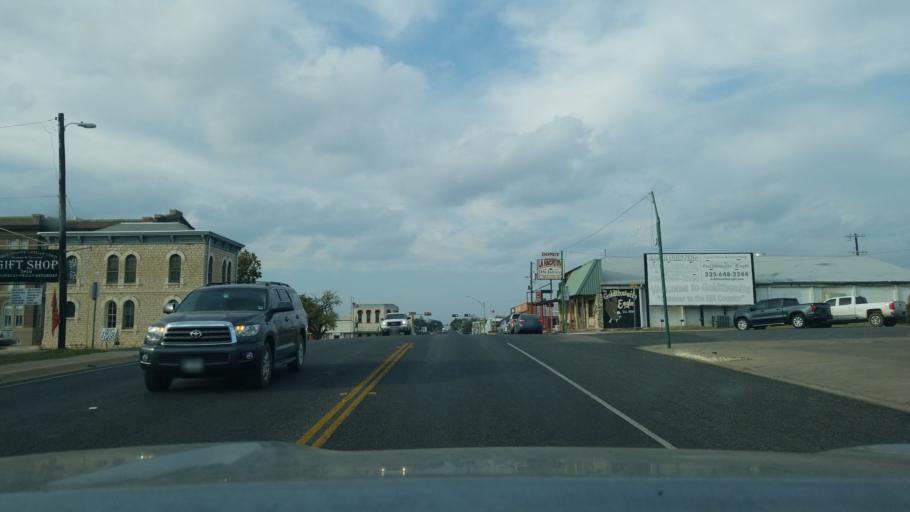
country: US
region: Texas
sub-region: Mills County
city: Goldthwaite
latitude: 31.4492
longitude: -98.5687
